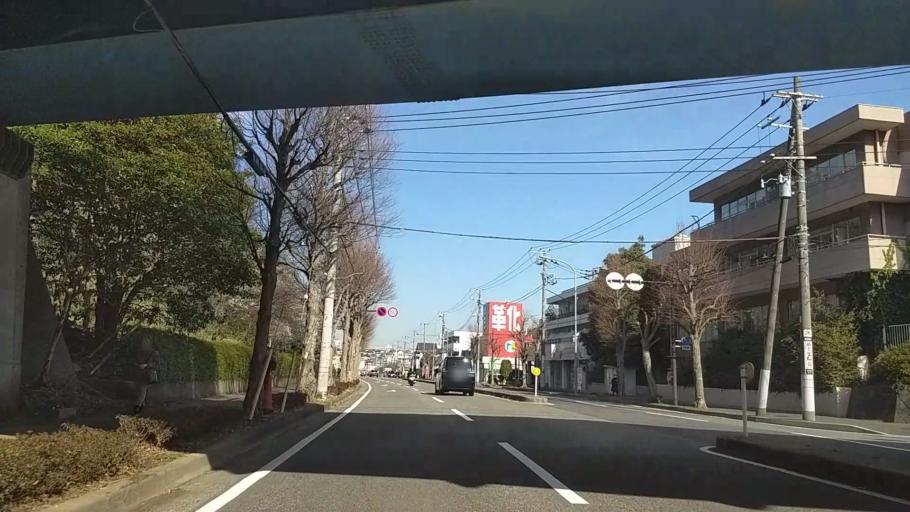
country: JP
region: Kanagawa
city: Kamakura
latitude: 35.3758
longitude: 139.5816
